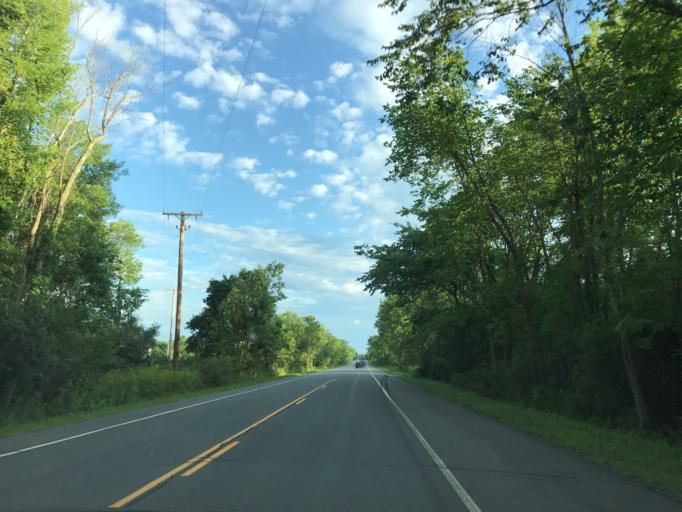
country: US
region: New York
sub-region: Saratoga County
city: Schuylerville
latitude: 43.0289
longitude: -73.5938
